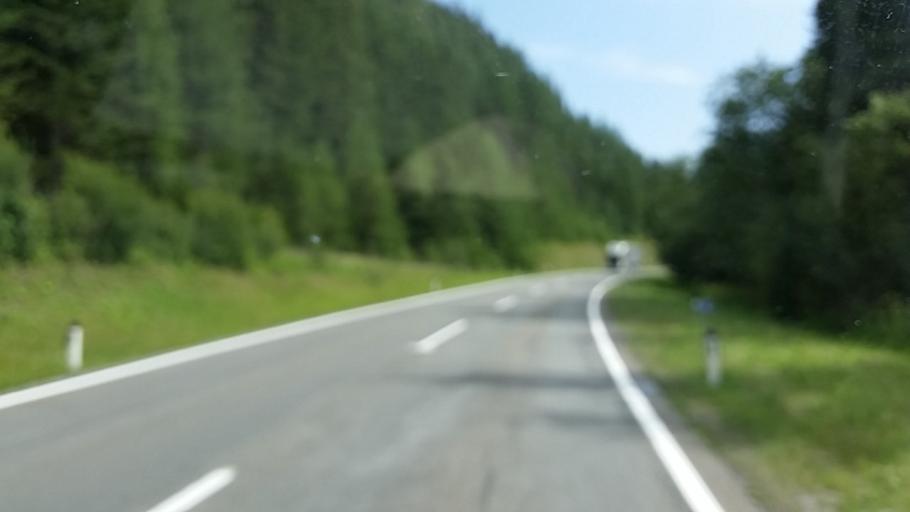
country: AT
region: Salzburg
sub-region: Politischer Bezirk Tamsweg
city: Mauterndorf
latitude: 47.1502
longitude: 13.6560
